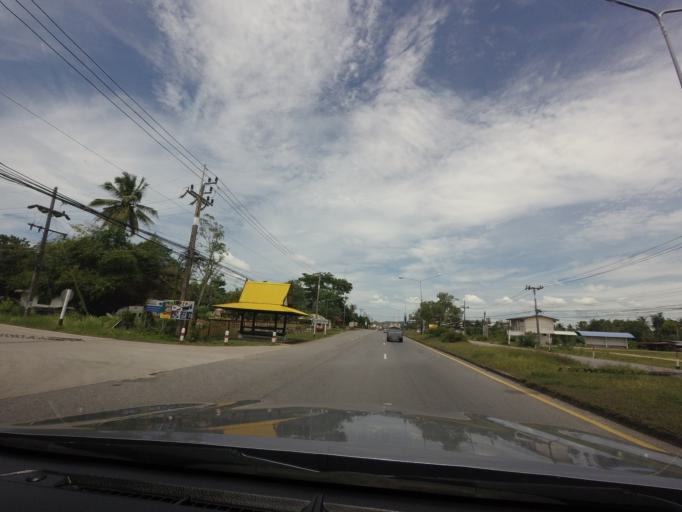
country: TH
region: Songkhla
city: Singhanakhon
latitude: 7.2400
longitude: 100.5485
